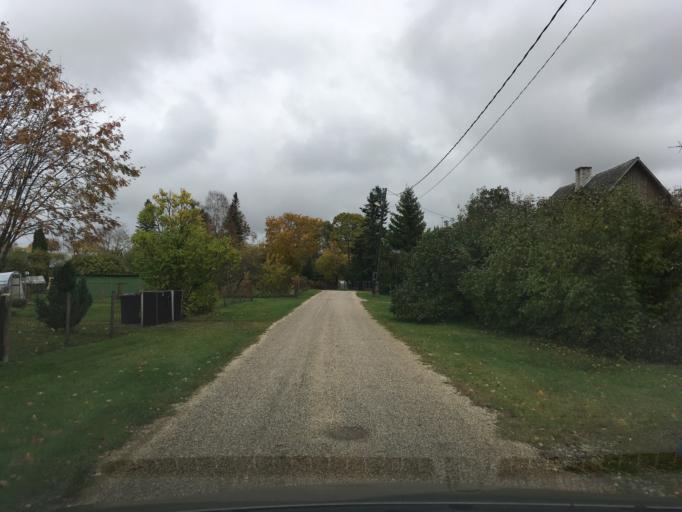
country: EE
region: Harju
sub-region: Raasiku vald
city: Raasiku
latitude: 59.1814
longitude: 25.1700
